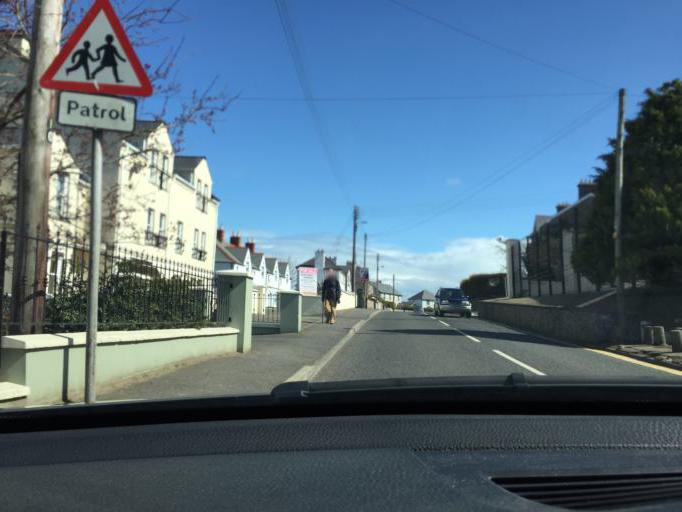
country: GB
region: Northern Ireland
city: Cushendall
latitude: 55.0801
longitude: -6.0608
